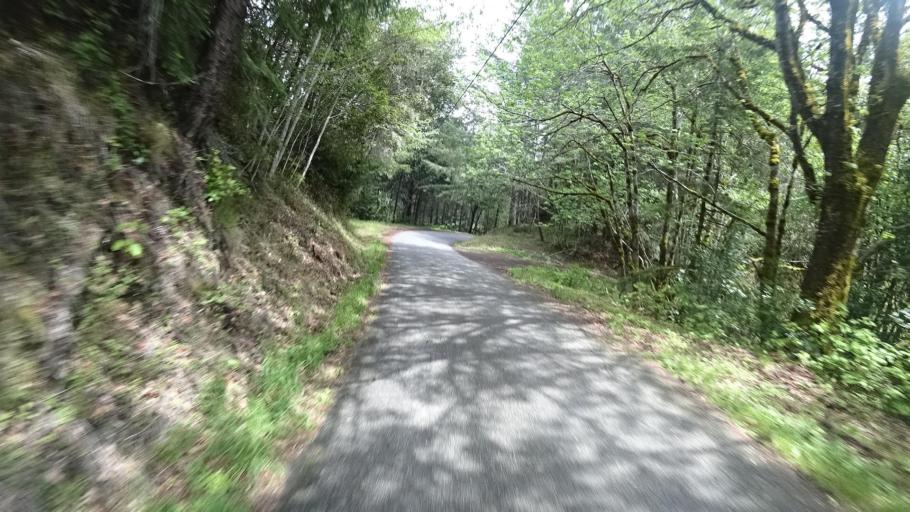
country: US
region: California
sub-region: Humboldt County
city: Blue Lake
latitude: 40.7600
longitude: -123.9119
